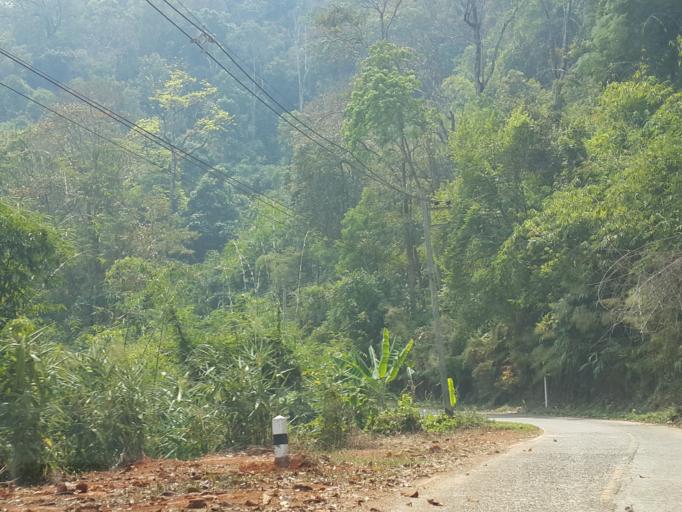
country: TH
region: Lampang
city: Mueang Pan
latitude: 18.8219
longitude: 99.4288
